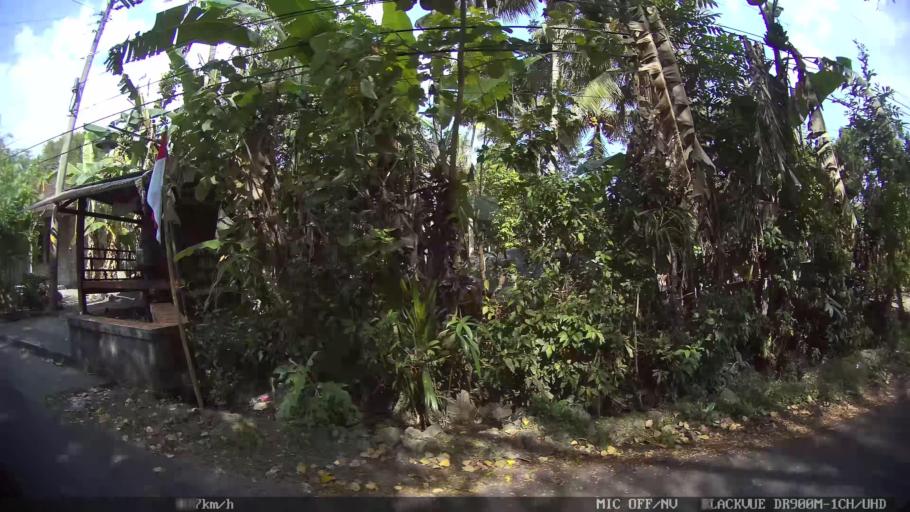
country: ID
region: Daerah Istimewa Yogyakarta
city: Kasihan
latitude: -7.8437
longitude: 110.3035
